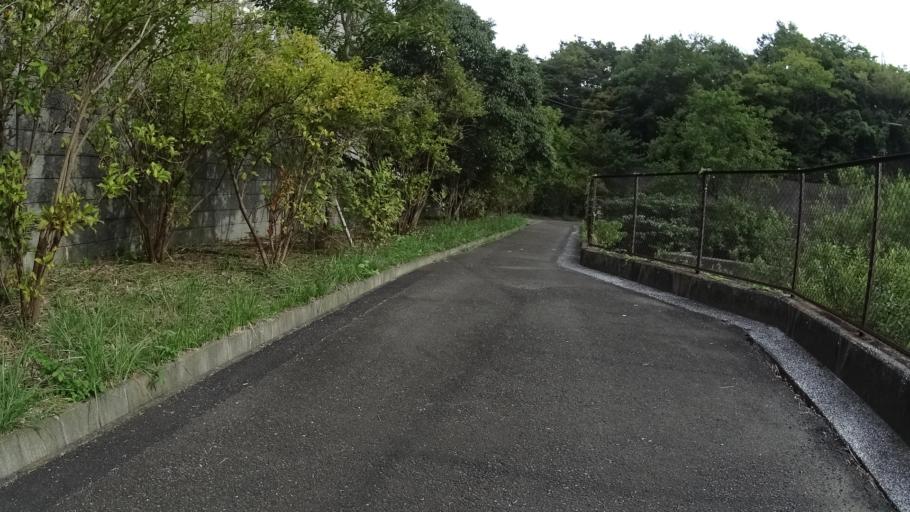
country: JP
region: Kanagawa
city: Zushi
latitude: 35.3538
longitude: 139.5978
